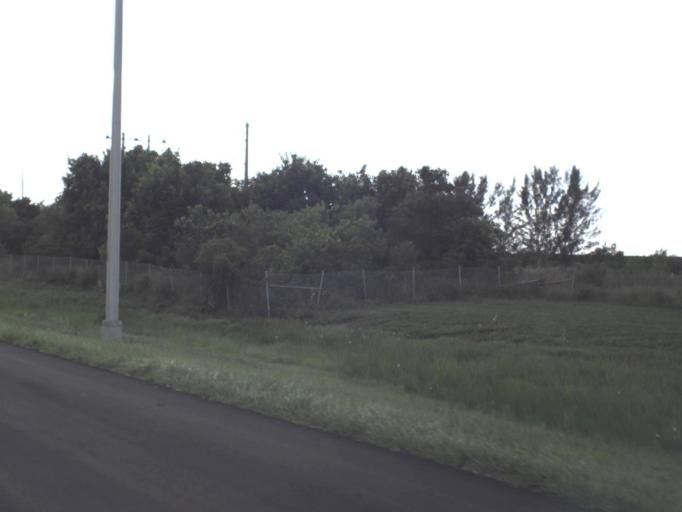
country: US
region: Florida
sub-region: Broward County
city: Tamarac
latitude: 26.2031
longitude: -80.2966
